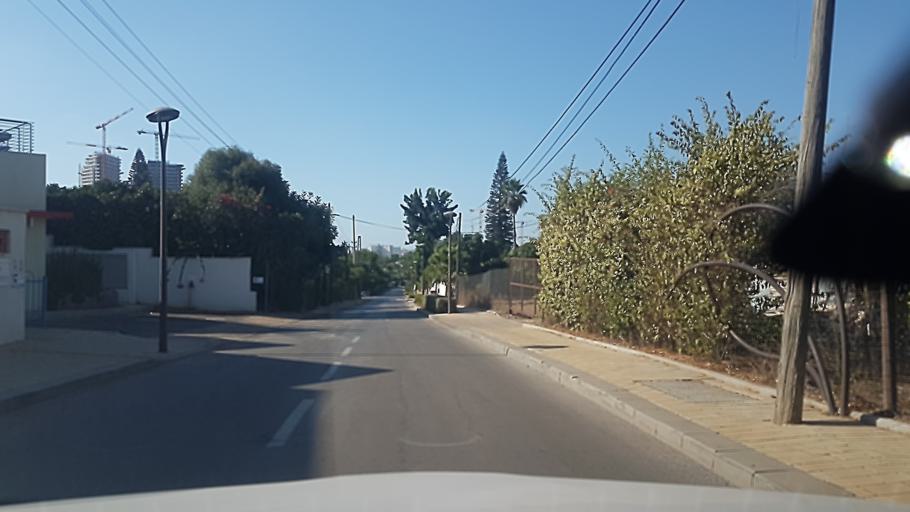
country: IL
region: Tel Aviv
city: Giv`at Shemu'el
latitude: 32.0553
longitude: 34.8429
